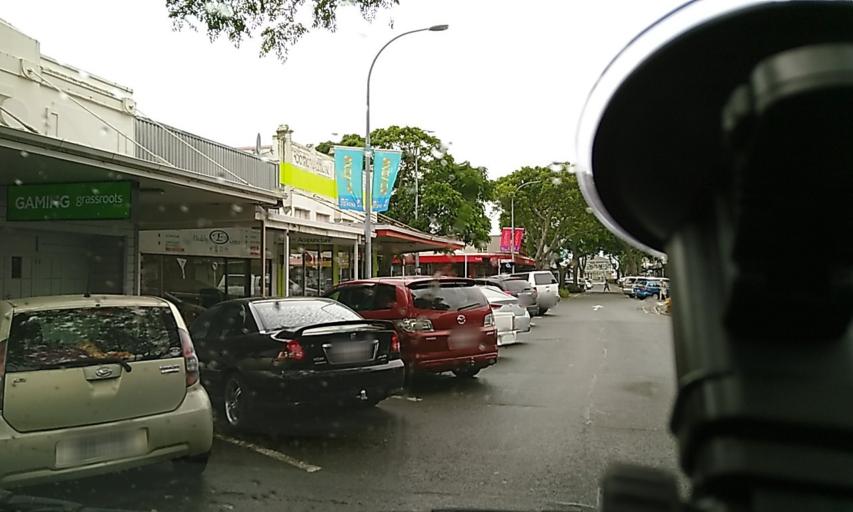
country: NZ
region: Waikato
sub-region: Hamilton City
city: Hamilton
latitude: -37.7878
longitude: 175.2650
